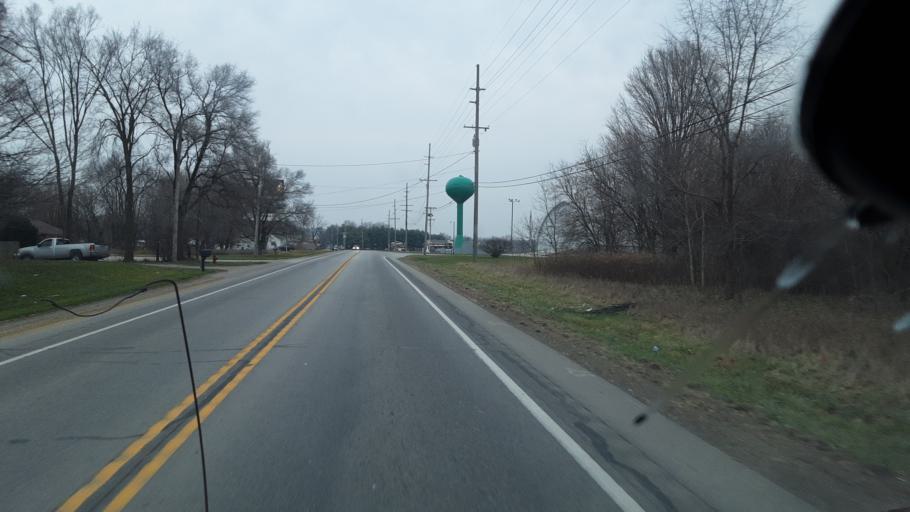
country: US
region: Indiana
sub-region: Elkhart County
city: Middlebury
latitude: 41.6940
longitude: -85.6938
